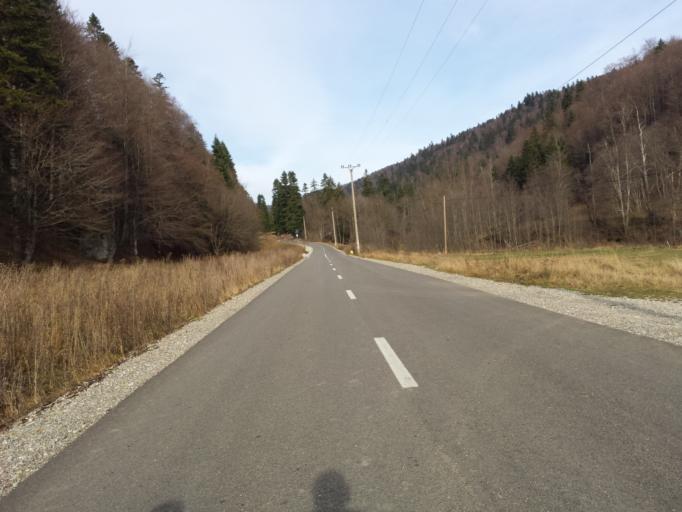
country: RO
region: Prahova
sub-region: Oras Azuga
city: Azuga
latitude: 45.4328
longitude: 25.5306
